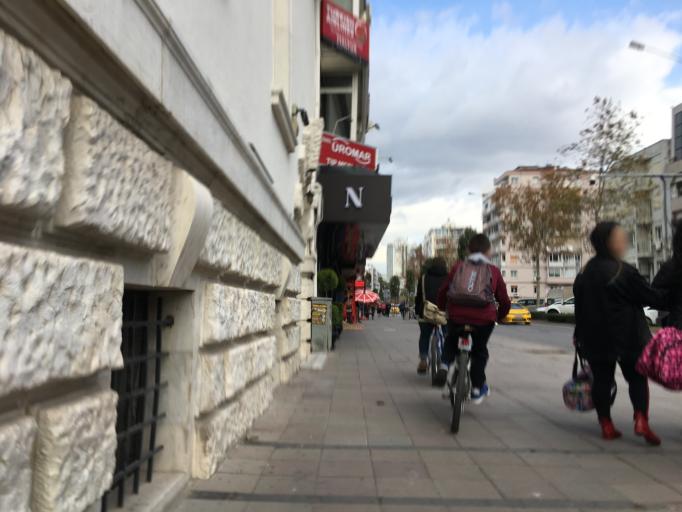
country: TR
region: Izmir
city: Izmir
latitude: 38.4318
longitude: 27.1368
